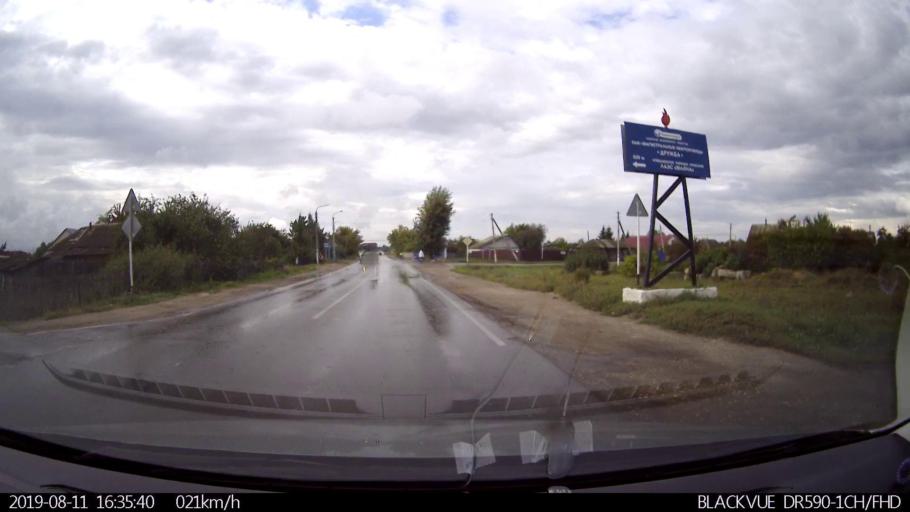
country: RU
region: Ulyanovsk
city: Mayna
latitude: 54.1155
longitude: 47.6149
